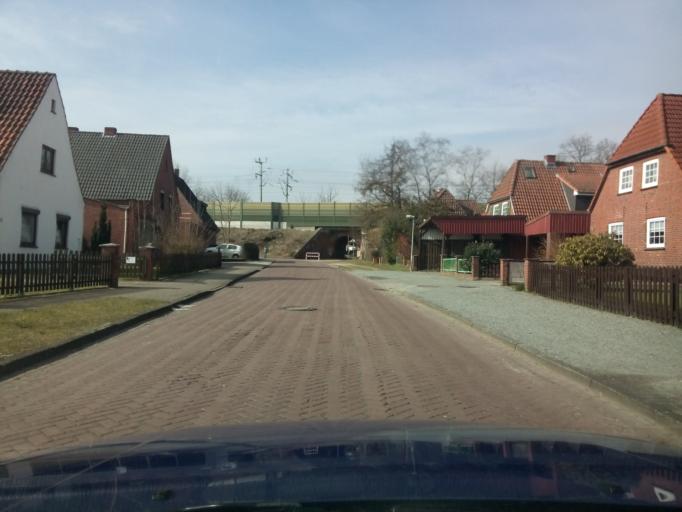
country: DE
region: Lower Saxony
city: Ritterhude
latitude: 53.1886
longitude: 8.7604
